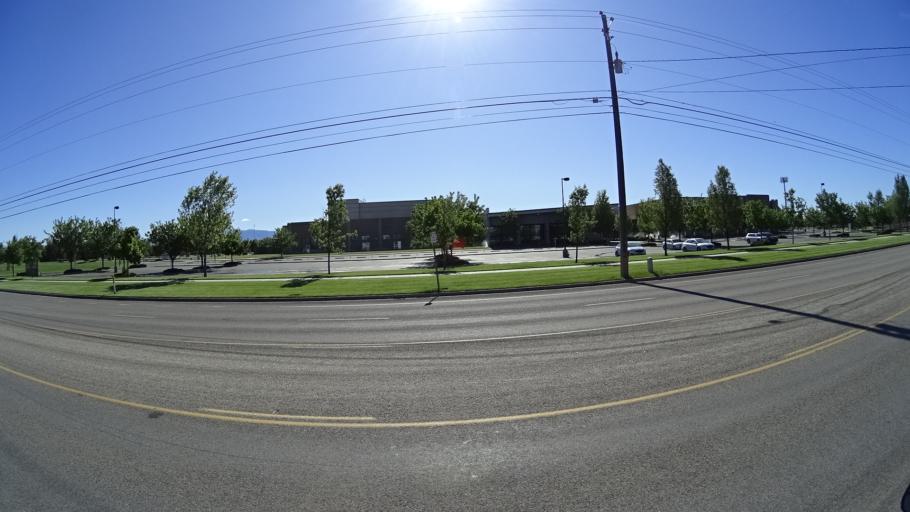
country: US
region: Idaho
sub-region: Ada County
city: Meridian
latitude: 43.6548
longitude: -116.4139
